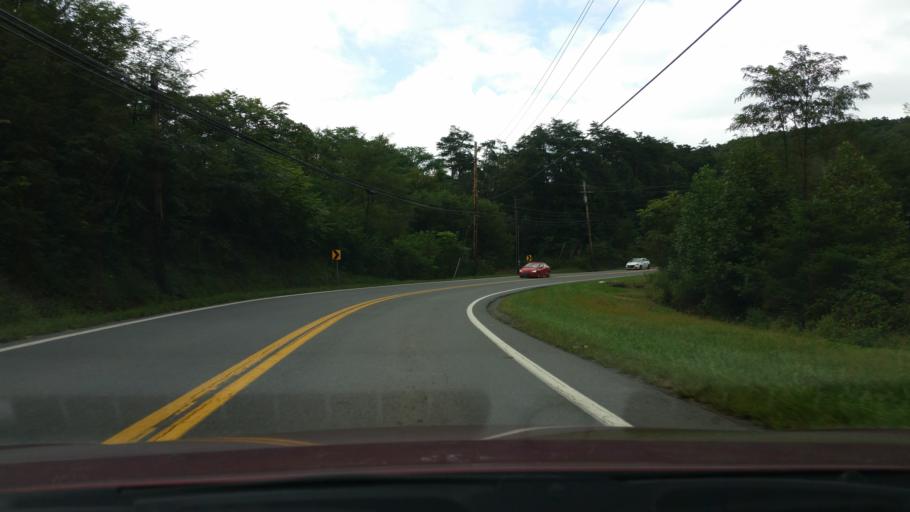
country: US
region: West Virginia
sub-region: Berkeley County
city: Martinsburg
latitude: 39.5578
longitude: -78.0027
